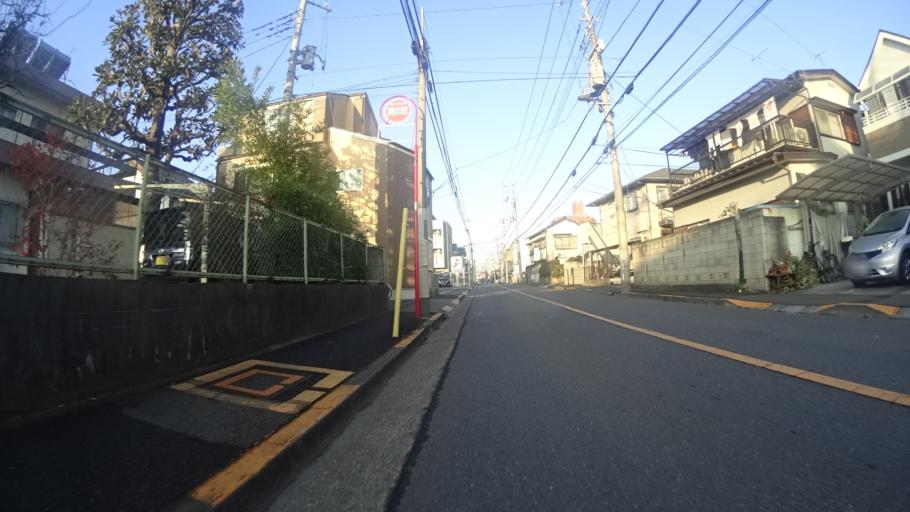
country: JP
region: Tokyo
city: Chofugaoka
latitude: 35.6679
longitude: 139.5094
